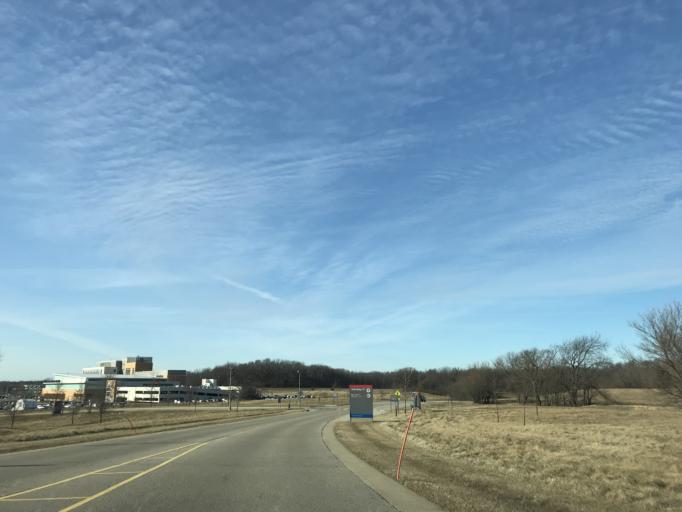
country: US
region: Wisconsin
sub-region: Dane County
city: Windsor
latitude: 43.1542
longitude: -89.2949
